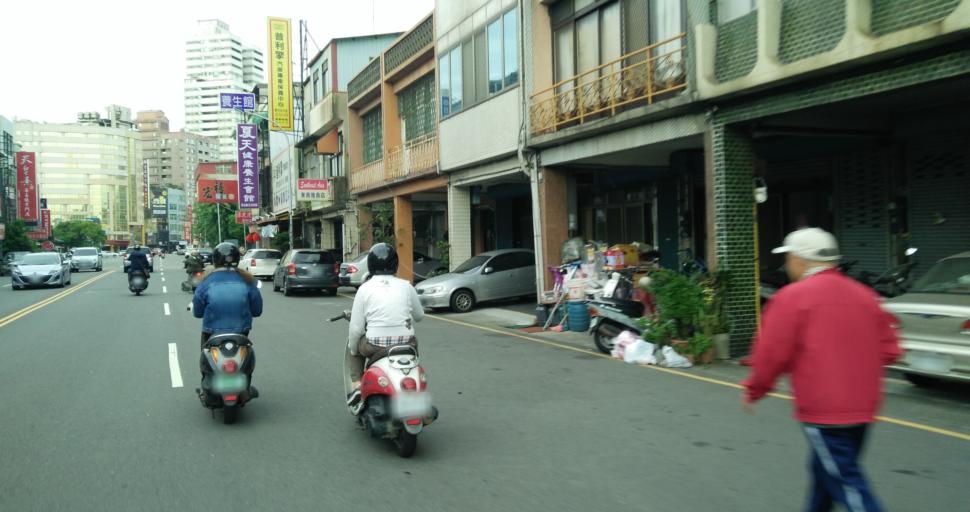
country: TW
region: Taiwan
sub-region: Hsinchu
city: Hsinchu
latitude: 24.8035
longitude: 120.9605
